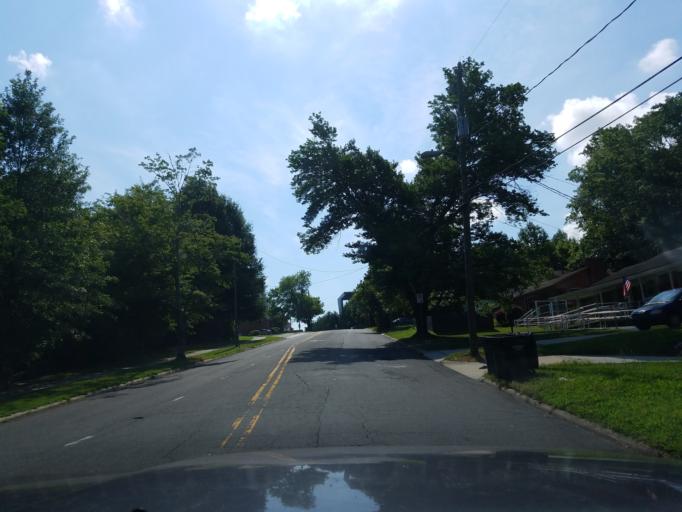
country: US
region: North Carolina
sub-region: Durham County
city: Durham
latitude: 35.9766
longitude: -78.9064
